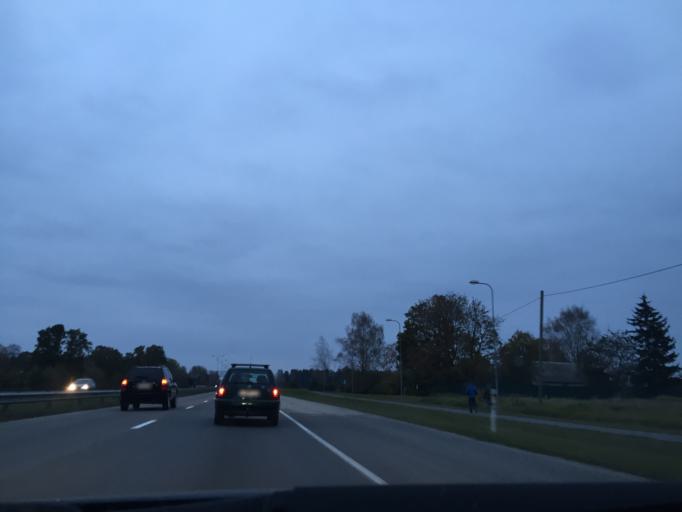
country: LV
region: Olaine
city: Olaine
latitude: 56.8044
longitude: 23.9890
